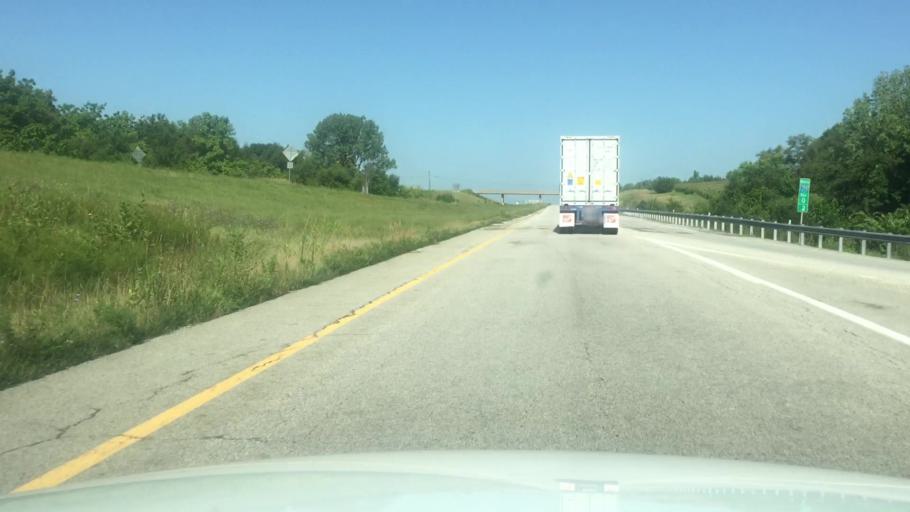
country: US
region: Missouri
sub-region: Buchanan County
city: Saint Joseph
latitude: 39.7087
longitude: -94.7915
